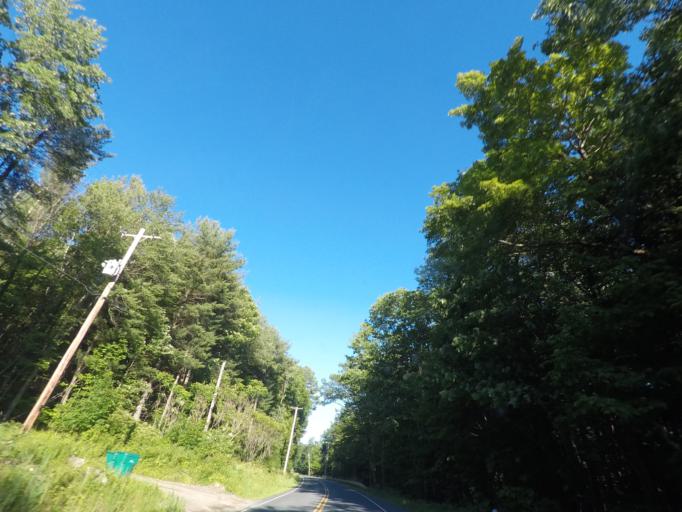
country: US
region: New York
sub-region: Rensselaer County
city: Averill Park
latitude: 42.5879
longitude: -73.5784
